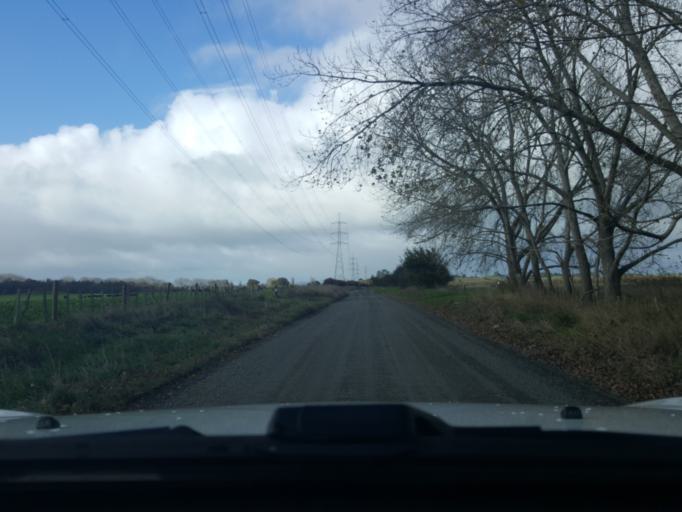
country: NZ
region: Waikato
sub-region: Waikato District
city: Te Kauwhata
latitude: -37.4132
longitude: 175.0626
